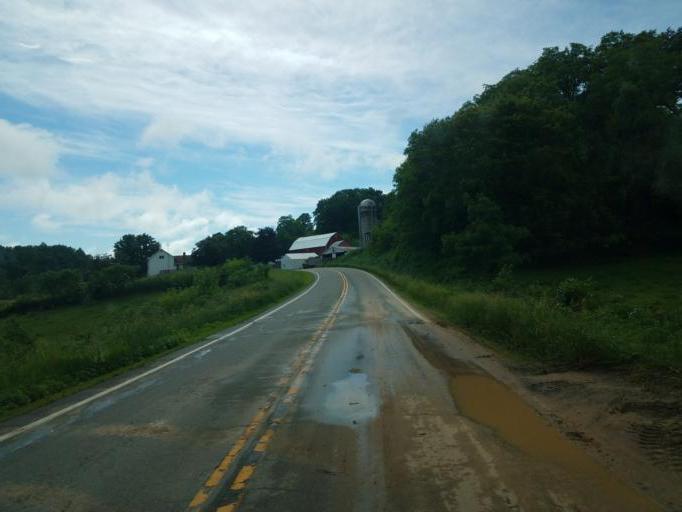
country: US
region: Wisconsin
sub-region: Vernon County
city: Hillsboro
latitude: 43.6613
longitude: -90.4367
